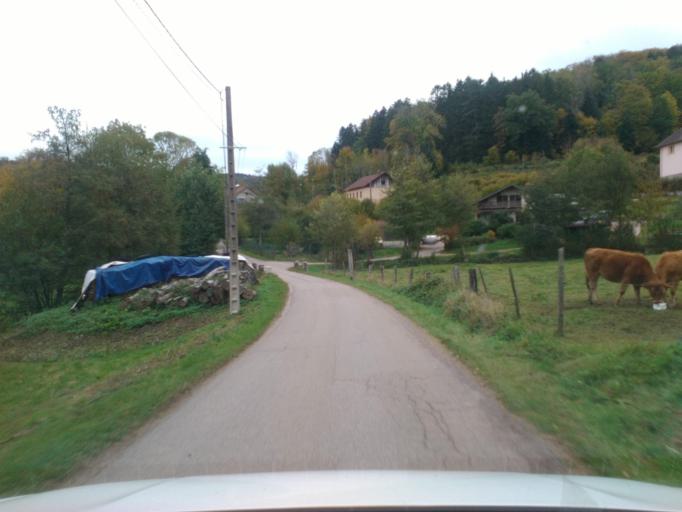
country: FR
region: Lorraine
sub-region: Departement des Vosges
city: Senones
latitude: 48.3334
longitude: 7.0174
